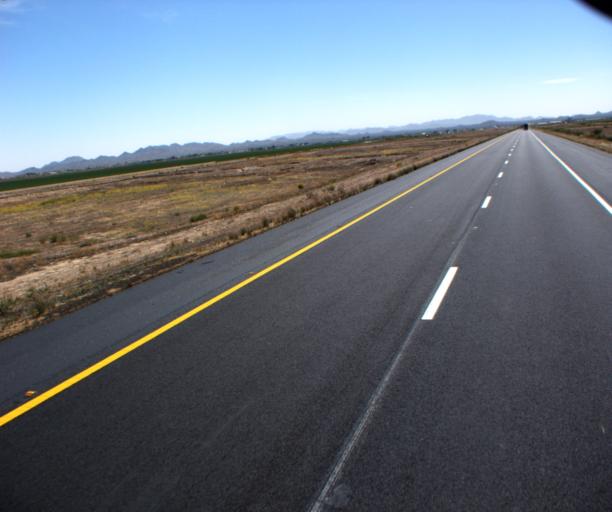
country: US
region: Arizona
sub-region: Maricopa County
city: Buckeye
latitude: 33.4017
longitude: -112.6270
